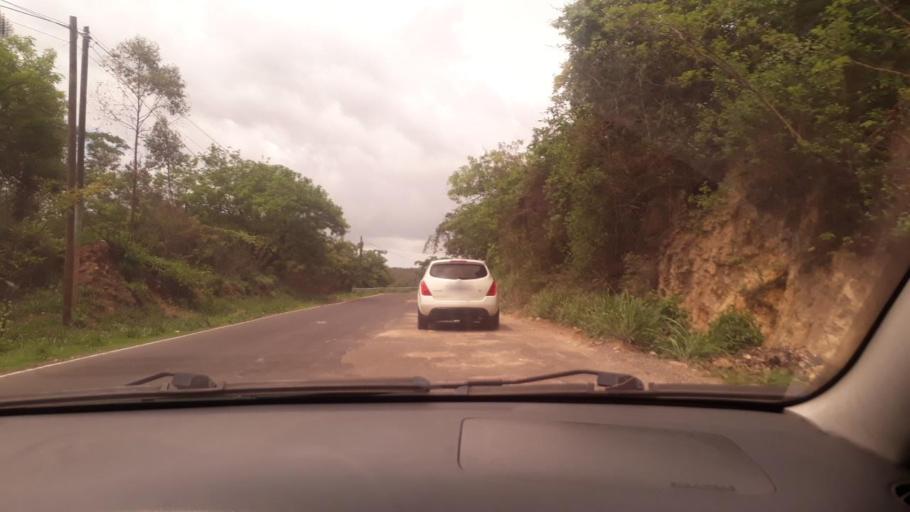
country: GT
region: Jutiapa
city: Quesada
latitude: 14.2773
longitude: -89.9908
